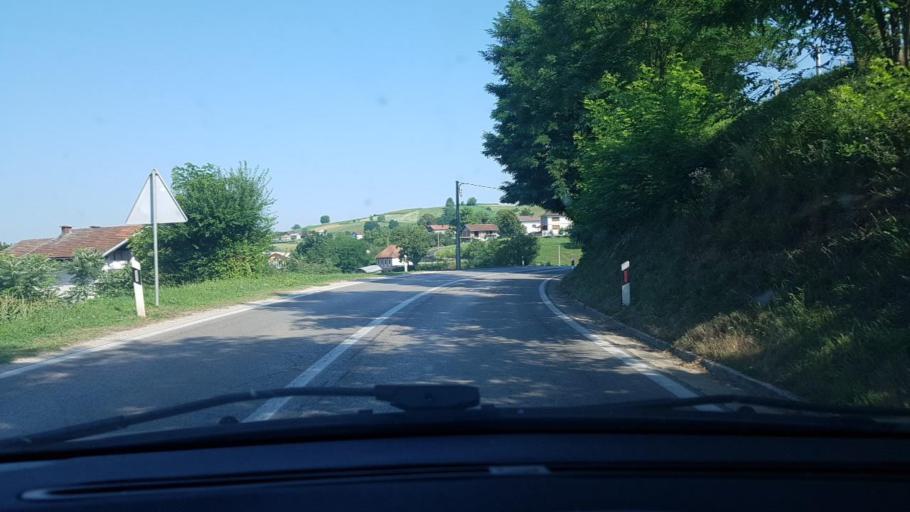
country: BA
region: Federation of Bosnia and Herzegovina
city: Mala Kladusa
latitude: 45.1289
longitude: 15.8662
